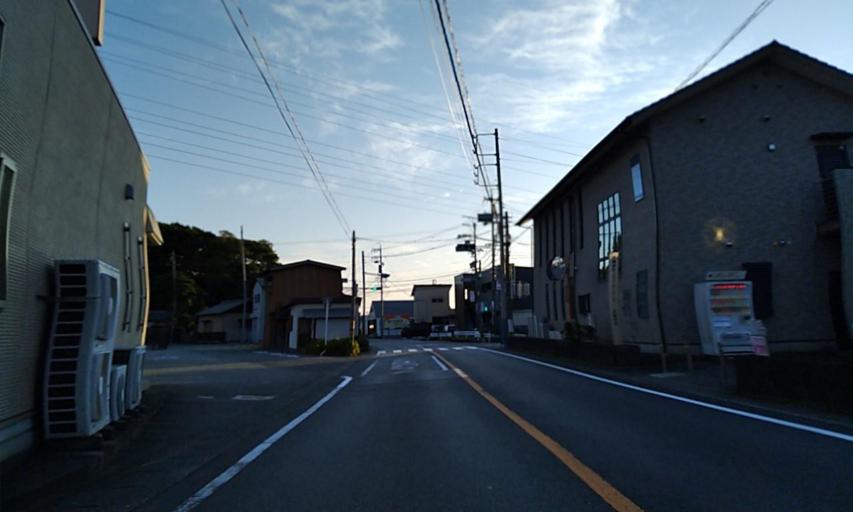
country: JP
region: Mie
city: Ise
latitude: 34.4963
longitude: 136.7284
